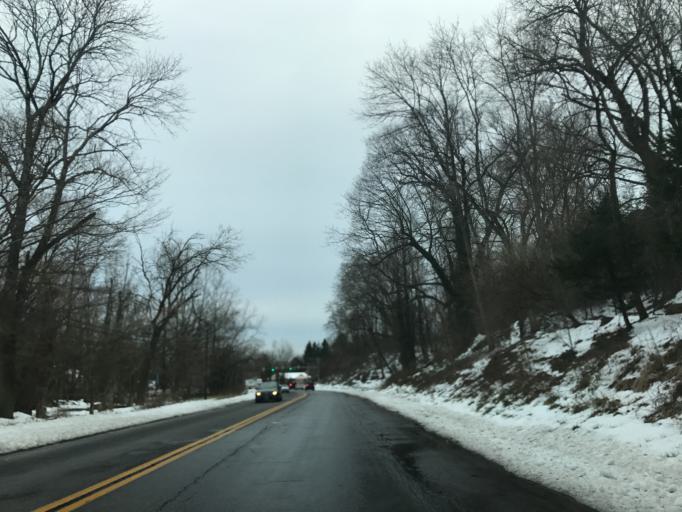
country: US
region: Maryland
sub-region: Baltimore County
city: Mays Chapel
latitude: 39.4109
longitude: -76.6487
